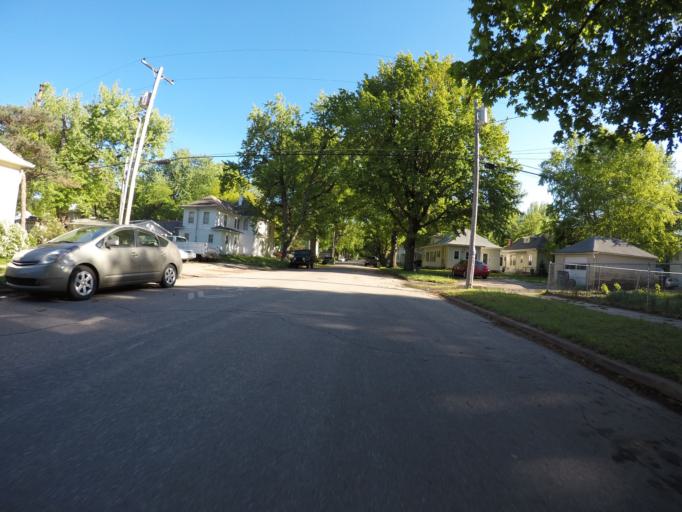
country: US
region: Kansas
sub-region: Riley County
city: Manhattan
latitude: 39.1832
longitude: -96.5685
